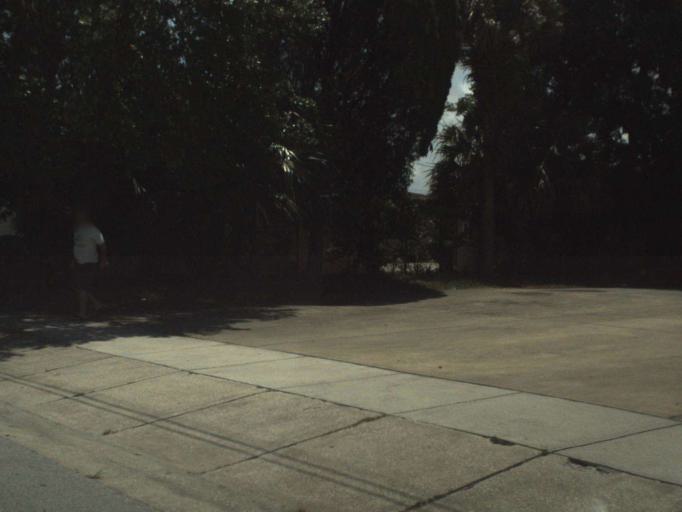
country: US
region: Florida
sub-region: Volusia County
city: Holly Hill
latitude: 29.2302
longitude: -81.0333
